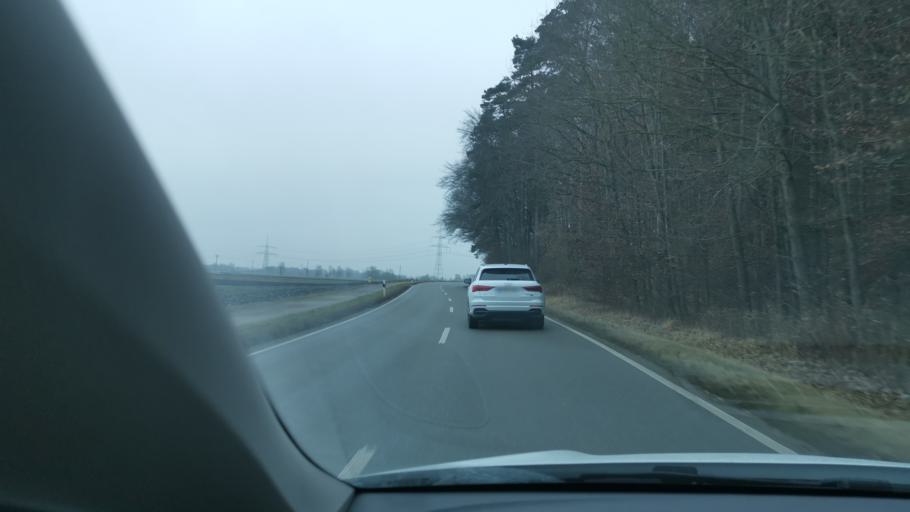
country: DE
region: Bavaria
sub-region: Swabia
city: Todtenweis
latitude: 48.5324
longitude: 10.9153
